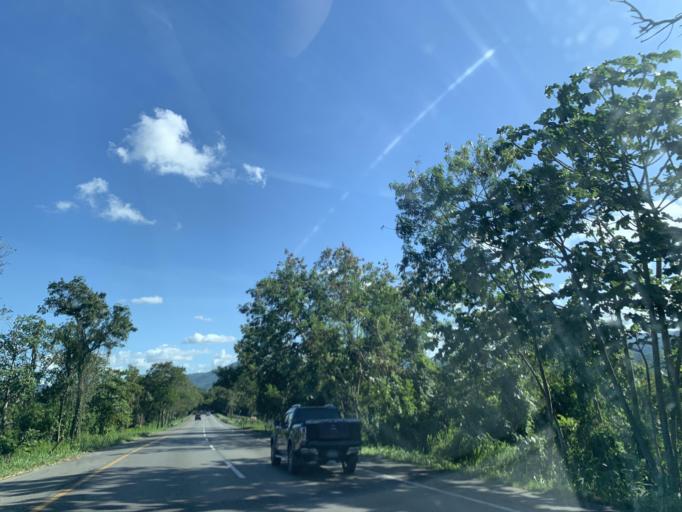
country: DO
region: San Cristobal
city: Villa Altagracia
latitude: 18.6520
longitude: -70.1664
